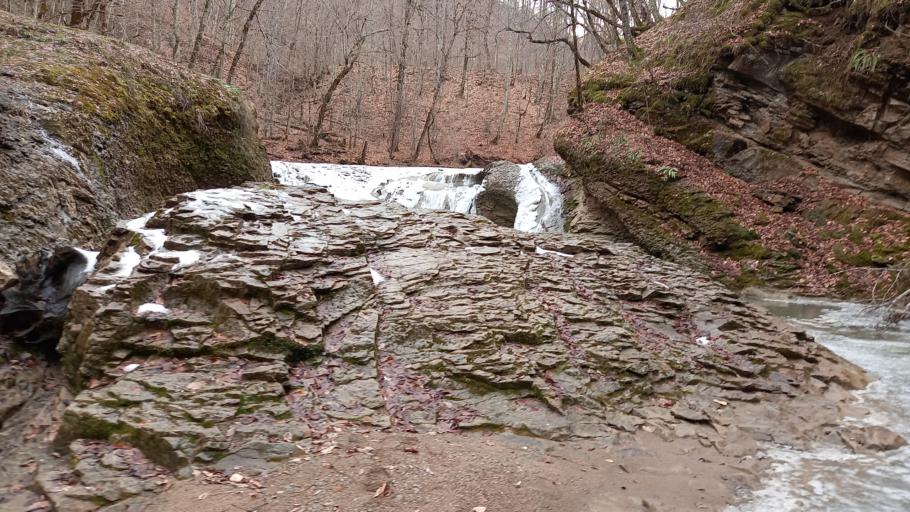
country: RU
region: Adygeya
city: Kamennomostskiy
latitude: 44.1747
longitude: 40.2994
